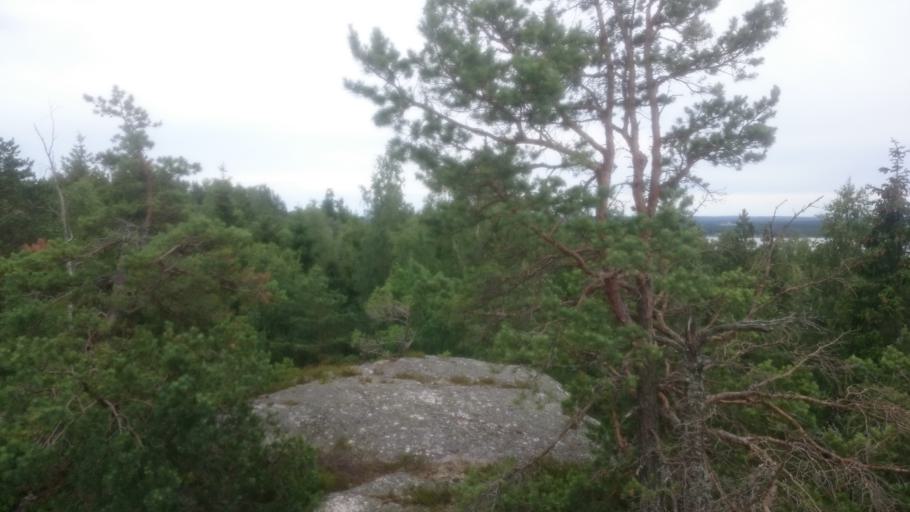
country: SE
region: OEstergoetland
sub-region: Norrkopings Kommun
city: Krokek
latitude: 58.6582
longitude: 16.4778
